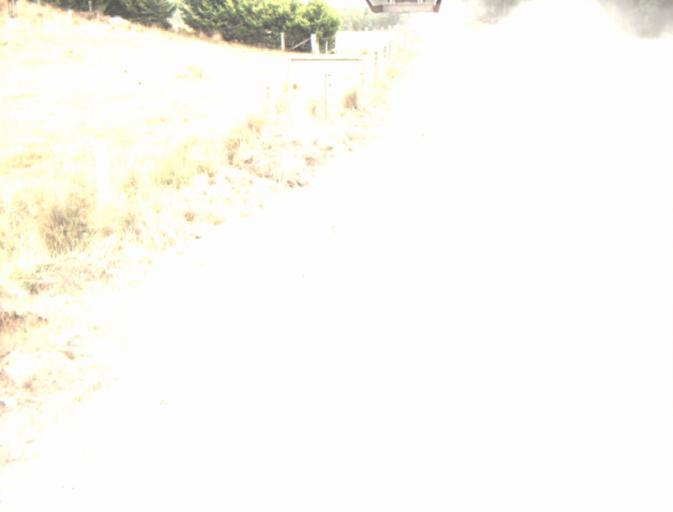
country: AU
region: Tasmania
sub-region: Dorset
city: Scottsdale
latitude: -41.3496
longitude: 147.4493
